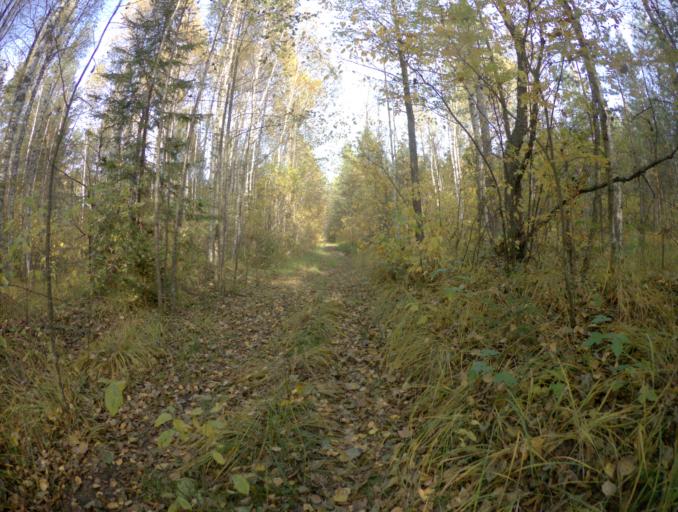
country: RU
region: Vladimir
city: Sobinka
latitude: 55.9353
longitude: 40.0423
